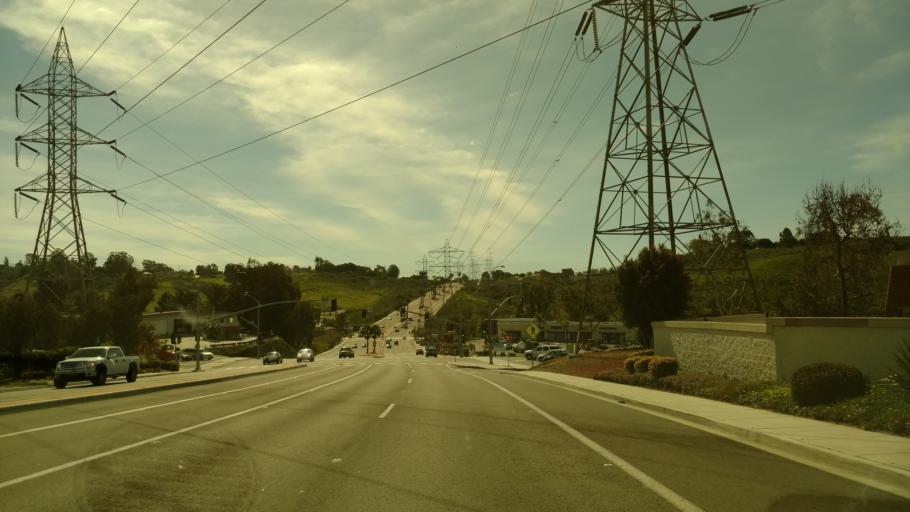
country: US
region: California
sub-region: San Diego County
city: Oceanside
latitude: 33.2026
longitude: -117.3330
